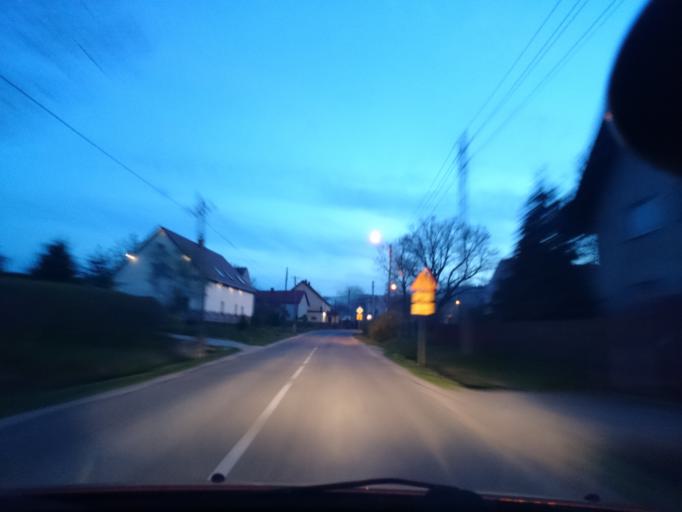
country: PL
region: Lower Silesian Voivodeship
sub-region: Powiat zabkowicki
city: Budzow
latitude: 50.5751
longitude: 16.6819
